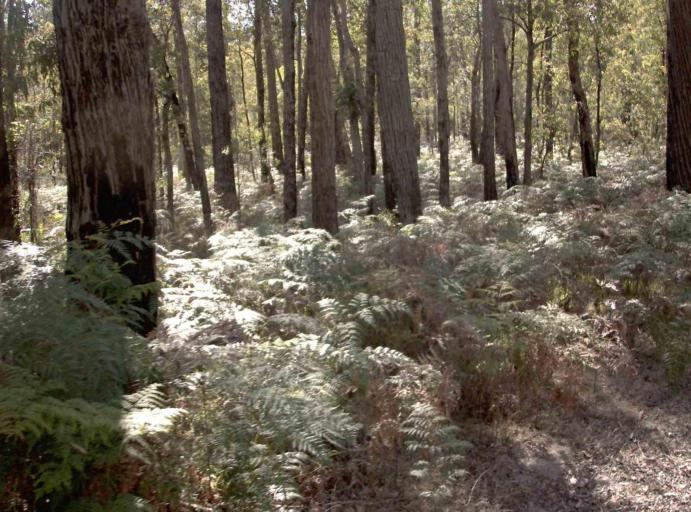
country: AU
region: New South Wales
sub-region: Bombala
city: Bombala
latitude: -37.3814
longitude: 148.6451
